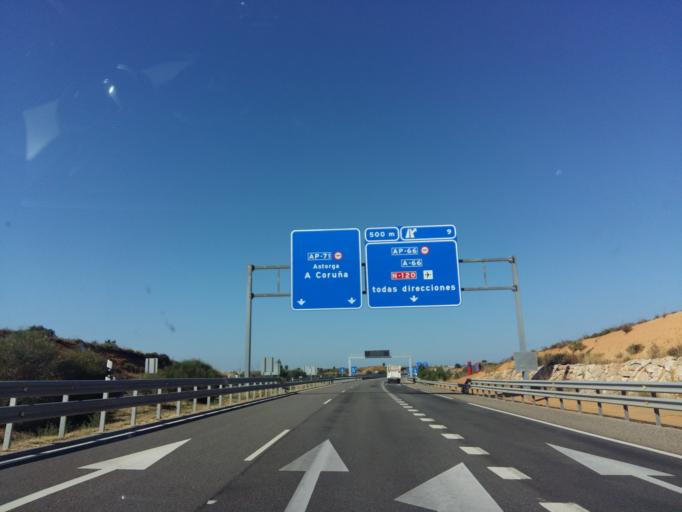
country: ES
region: Castille and Leon
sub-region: Provincia de Leon
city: San Andres del Rabanedo
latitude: 42.5727
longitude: -5.6347
